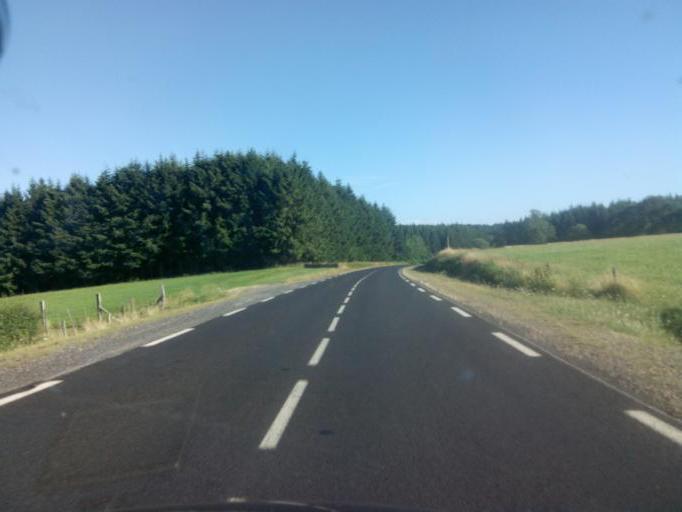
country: FR
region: Auvergne
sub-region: Departement de la Haute-Loire
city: Fontannes
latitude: 45.3059
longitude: 3.7006
